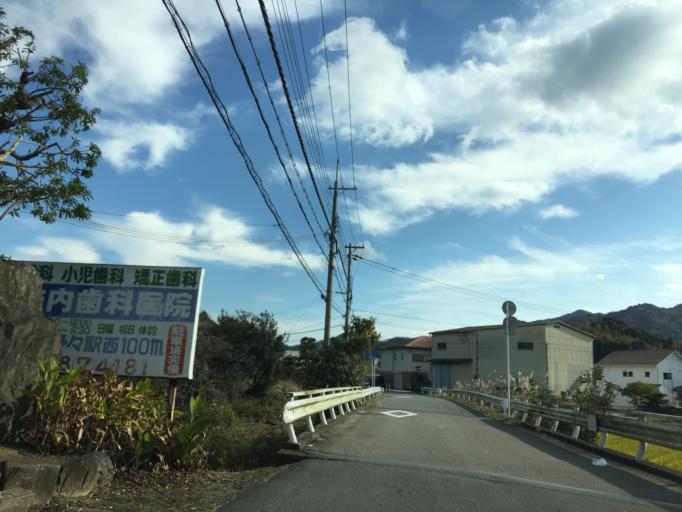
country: JP
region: Wakayama
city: Kainan
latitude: 34.1591
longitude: 135.2684
